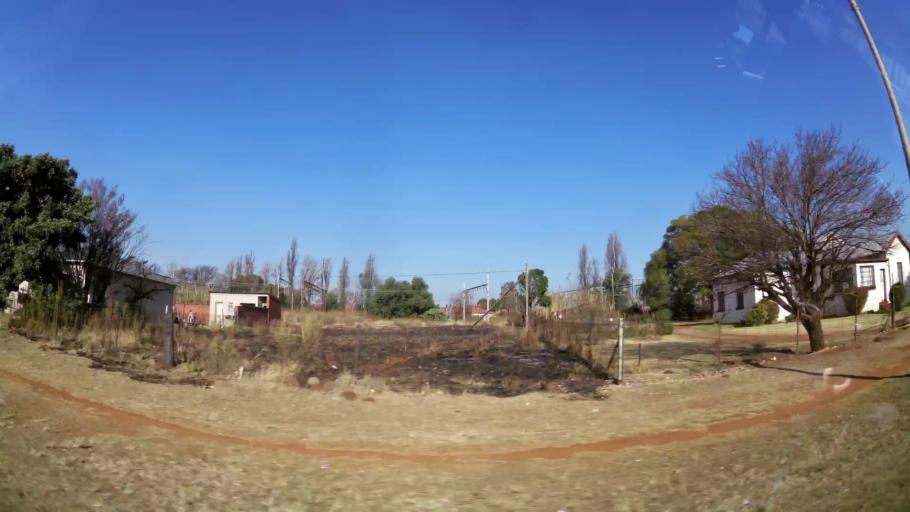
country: ZA
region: Gauteng
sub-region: West Rand District Municipality
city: Randfontein
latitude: -26.1587
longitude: 27.7131
